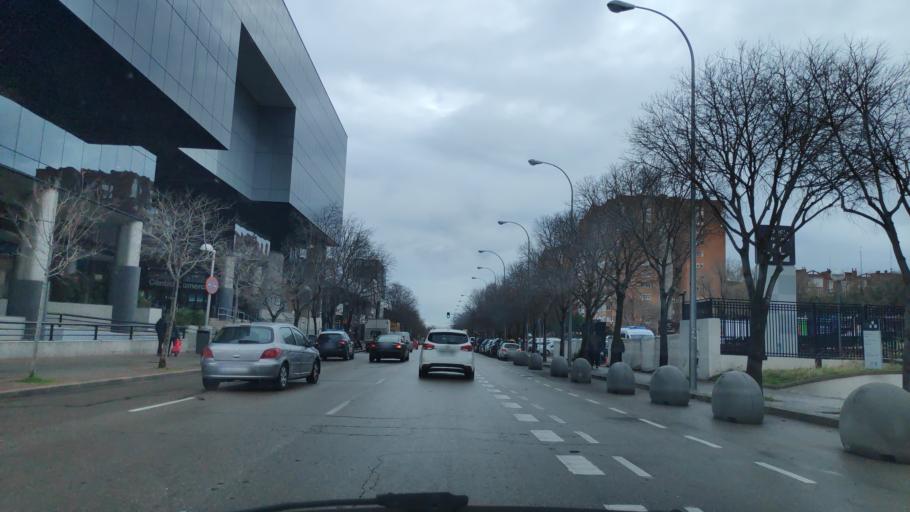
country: ES
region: Madrid
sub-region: Provincia de Madrid
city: Hortaleza
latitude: 40.4691
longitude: -3.6416
